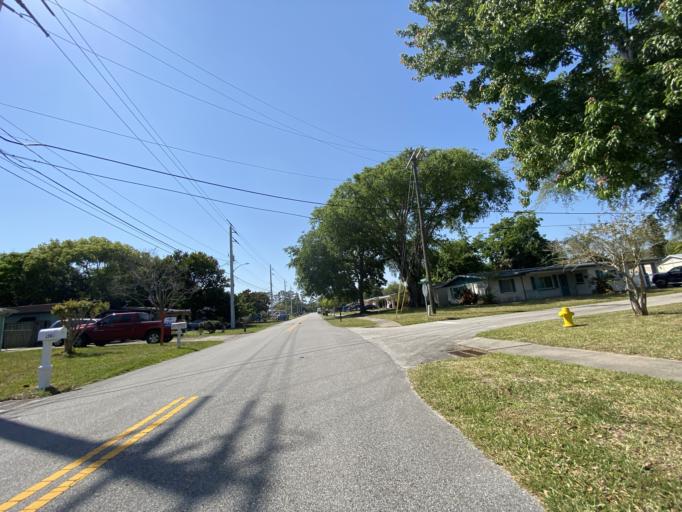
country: US
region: Florida
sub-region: Volusia County
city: South Daytona
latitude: 29.1610
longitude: -81.0026
